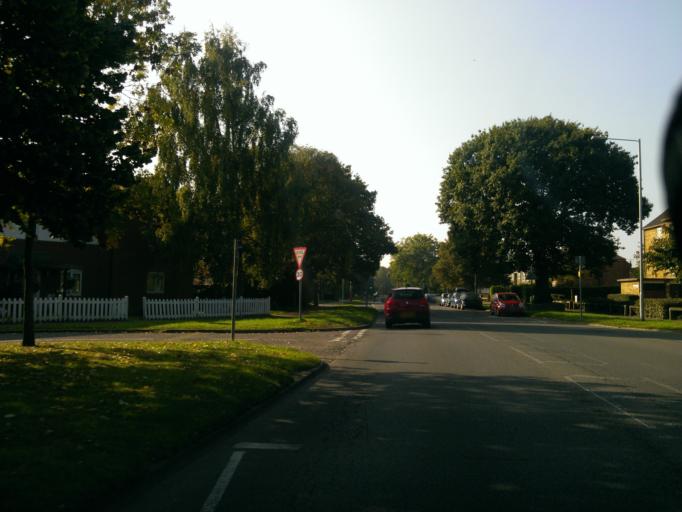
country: GB
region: England
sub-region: Essex
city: Layer de la Haye
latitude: 51.8707
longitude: 0.8767
